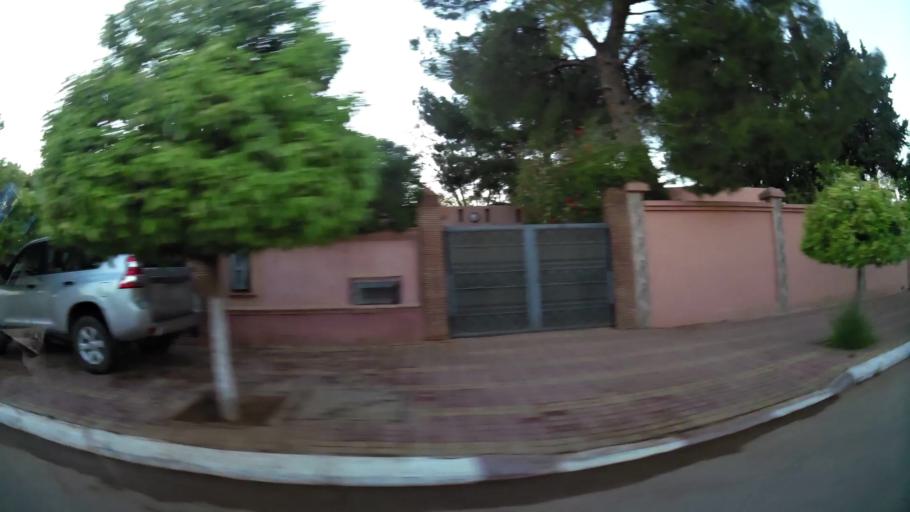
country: MA
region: Marrakech-Tensift-Al Haouz
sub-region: Kelaa-Des-Sraghna
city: Sidi Bou Othmane
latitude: 32.2121
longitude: -7.9312
